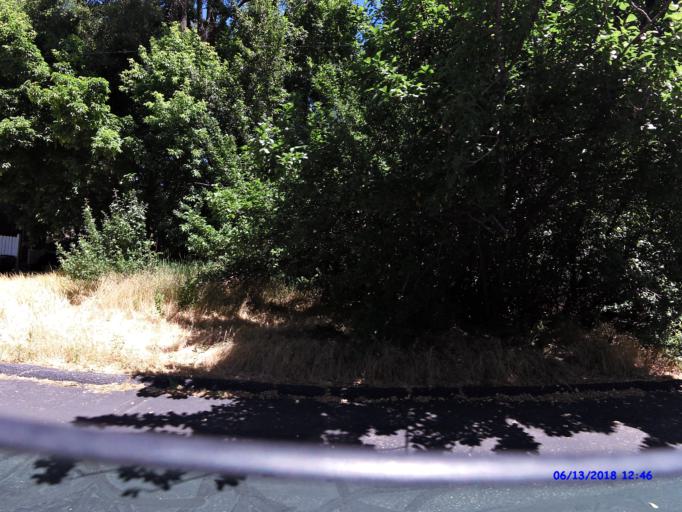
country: US
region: Utah
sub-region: Weber County
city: South Ogden
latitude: 41.2055
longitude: -111.9511
